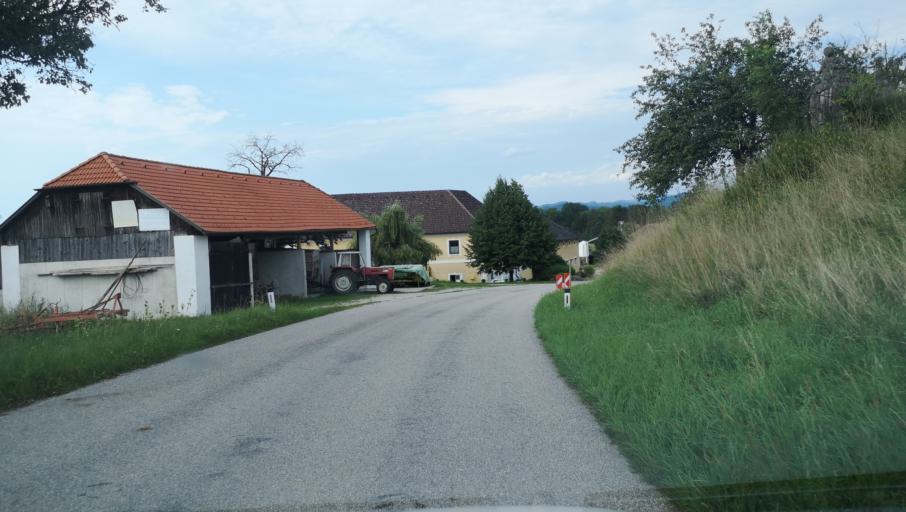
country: AT
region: Lower Austria
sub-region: Politischer Bezirk Amstetten
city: Zeillern
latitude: 48.1521
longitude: 14.8256
